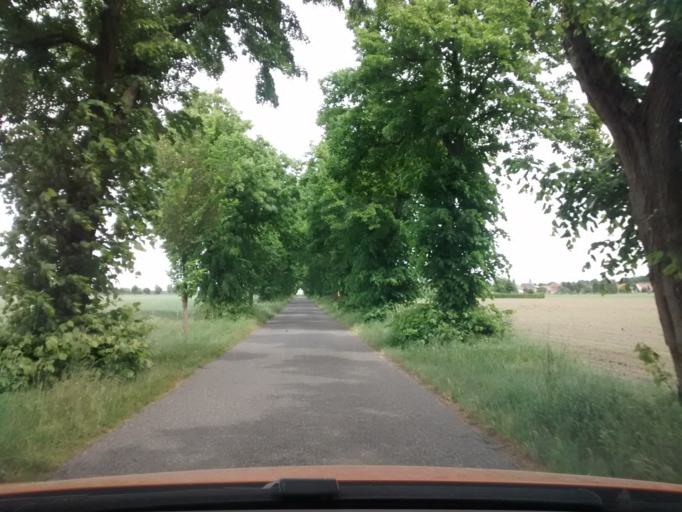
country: DE
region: Saxony-Anhalt
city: Holzdorf
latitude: 51.8391
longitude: 13.2083
